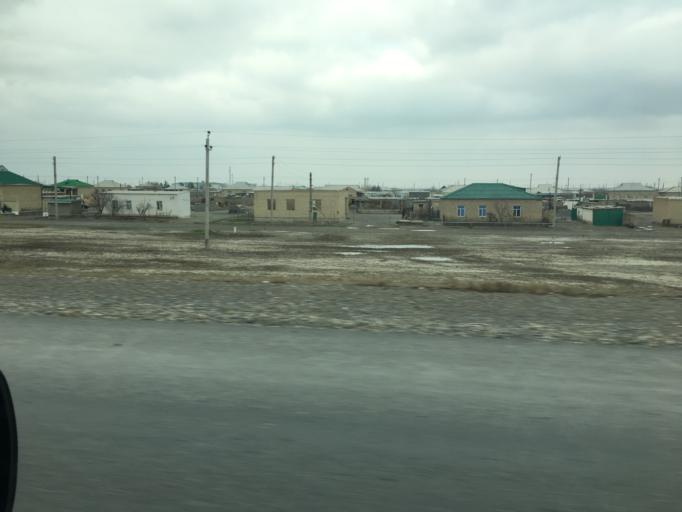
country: TM
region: Ahal
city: Kaka
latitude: 37.2969
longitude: 59.7787
